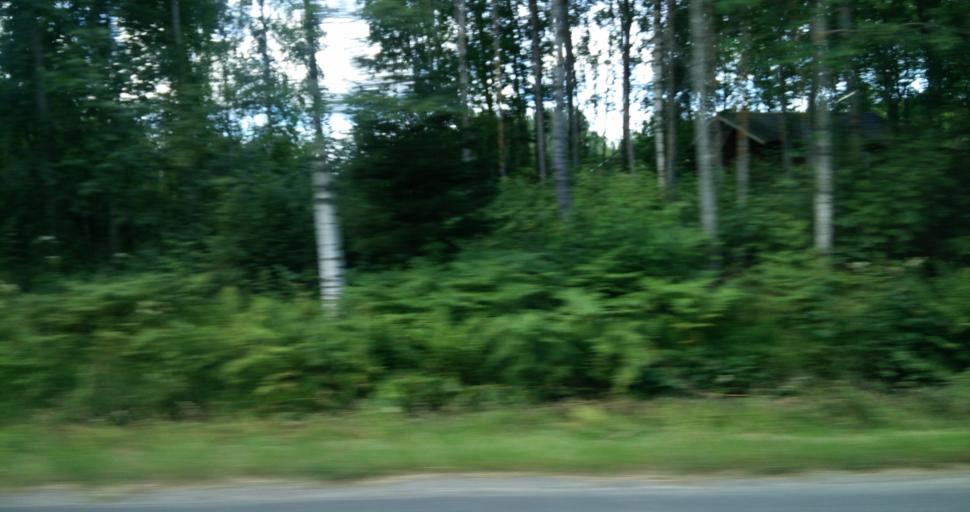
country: SE
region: Vaermland
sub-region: Hagfors Kommun
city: Ekshaerad
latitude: 60.1370
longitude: 13.4591
